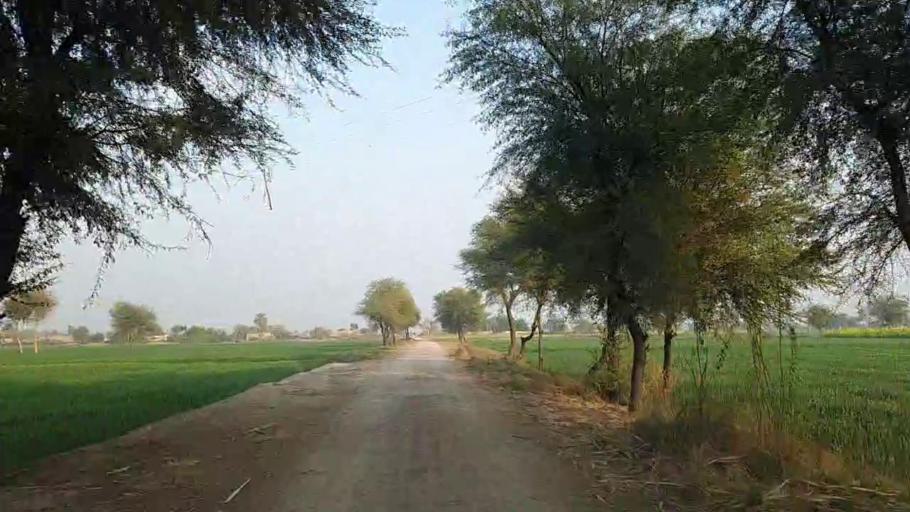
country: PK
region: Sindh
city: Jam Sahib
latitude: 26.3254
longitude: 68.5679
